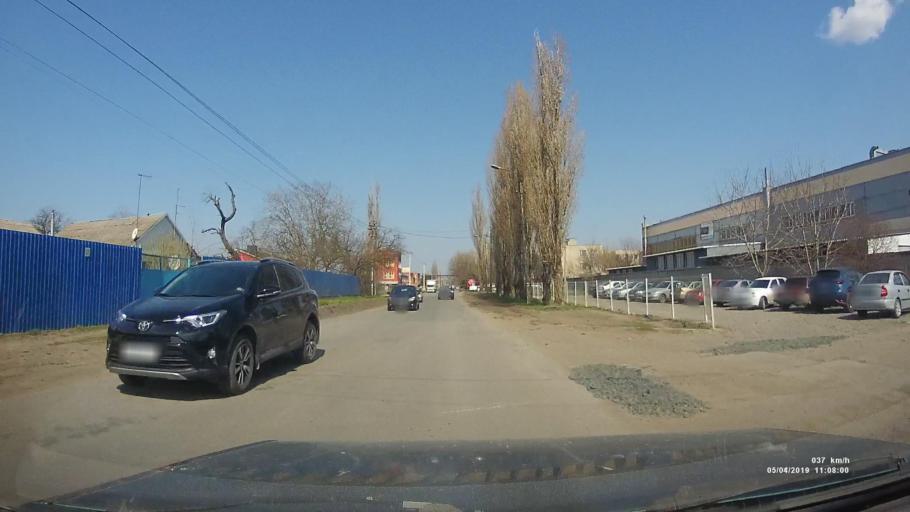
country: RU
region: Rostov
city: Azov
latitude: 47.0839
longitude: 39.4366
